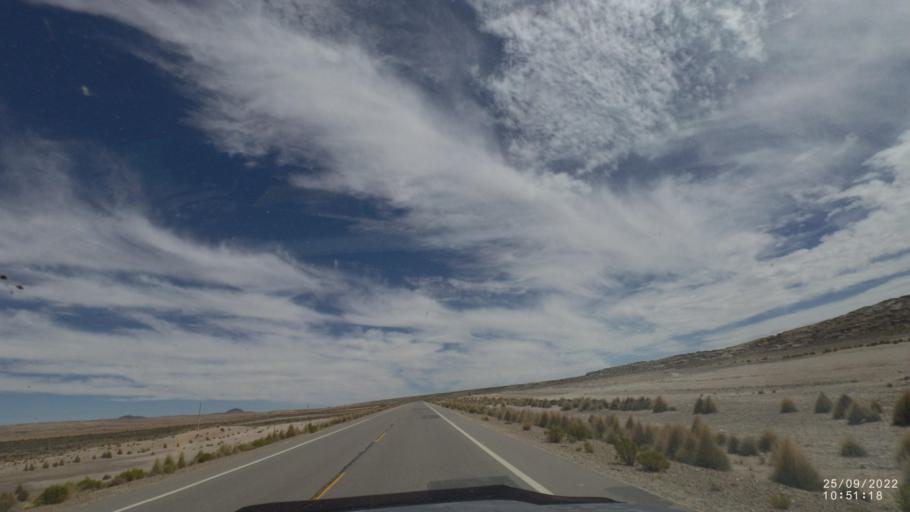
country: BO
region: Oruro
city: Challapata
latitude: -19.5638
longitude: -66.8467
